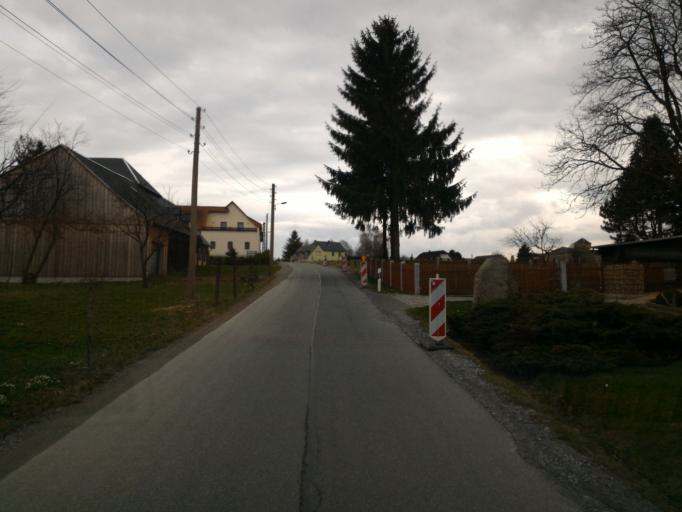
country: DE
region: Saxony
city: Ebersbach
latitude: 51.0038
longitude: 14.6047
